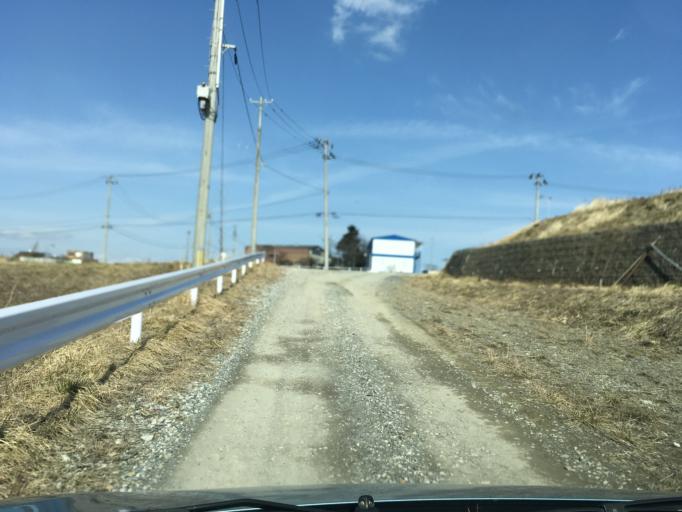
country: JP
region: Iwate
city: Ofunato
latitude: 38.8278
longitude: 141.5853
